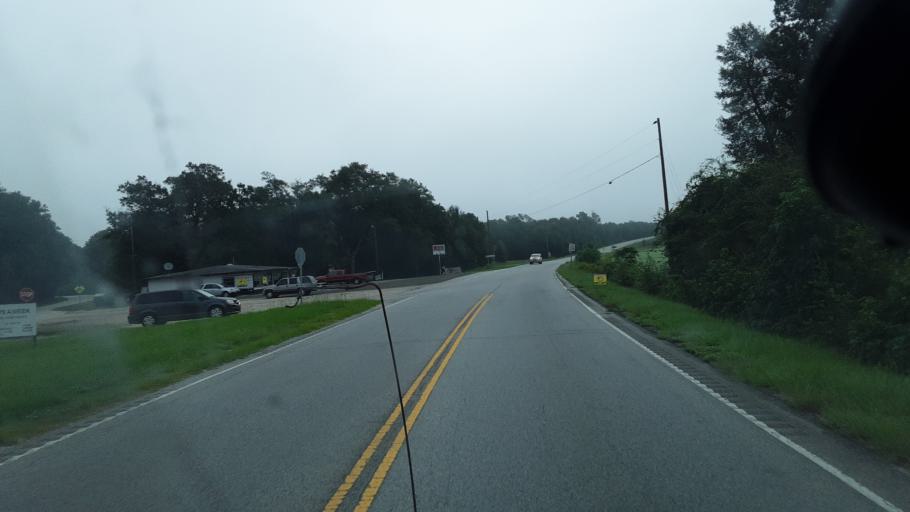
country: US
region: South Carolina
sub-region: Florence County
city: Johnsonville
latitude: 33.9138
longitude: -79.4198
